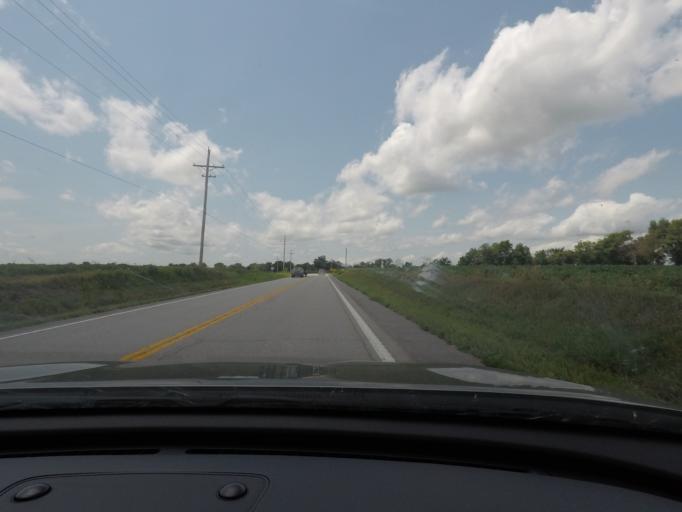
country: US
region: Missouri
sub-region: Carroll County
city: Carrollton
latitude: 39.1952
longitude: -93.4016
